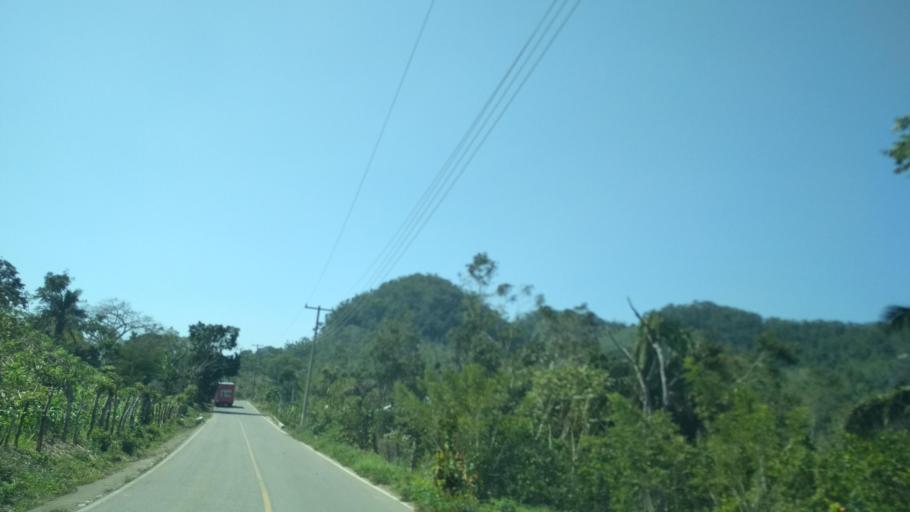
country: MX
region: Veracruz
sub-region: Papantla
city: Polutla
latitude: 20.4743
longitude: -97.2158
